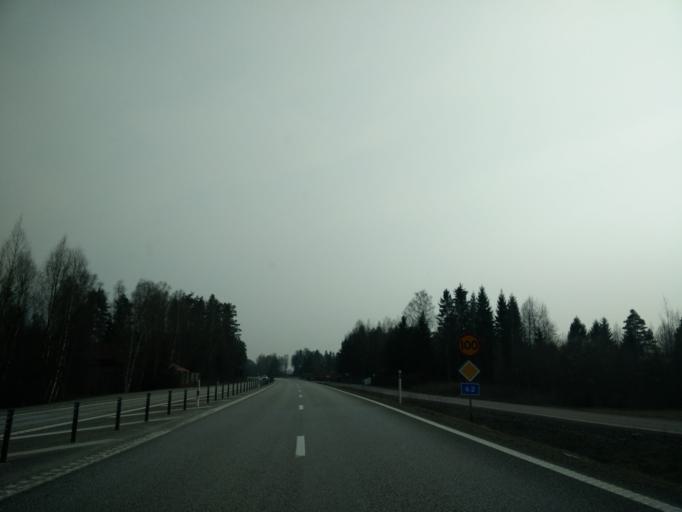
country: SE
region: Vaermland
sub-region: Forshaga Kommun
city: Forshaga
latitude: 59.4808
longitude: 13.4115
